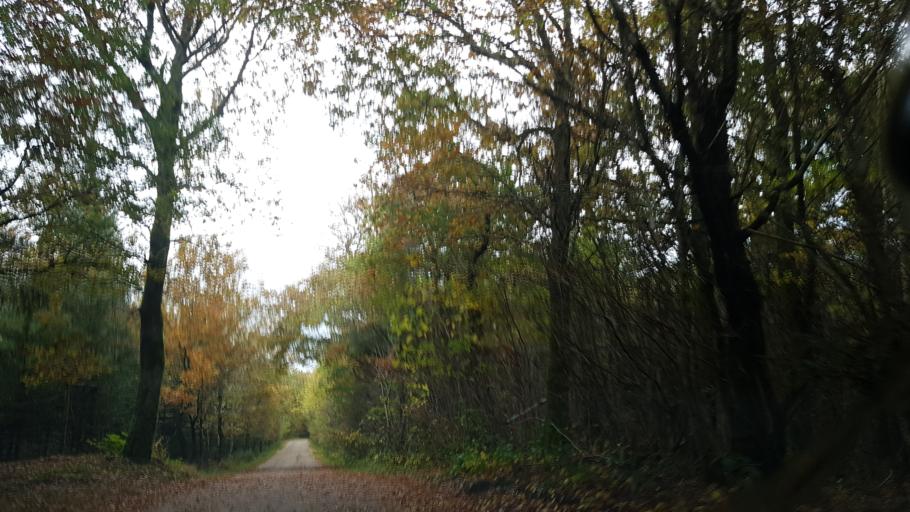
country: DK
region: South Denmark
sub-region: Tonder Kommune
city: Sherrebek
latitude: 55.1752
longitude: 8.7654
